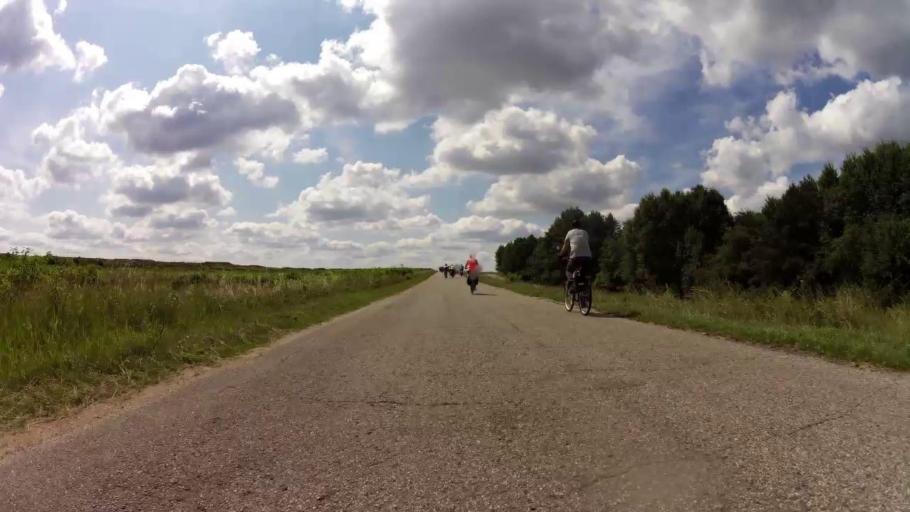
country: PL
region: West Pomeranian Voivodeship
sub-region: Powiat drawski
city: Drawsko Pomorskie
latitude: 53.4459
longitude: 15.7625
